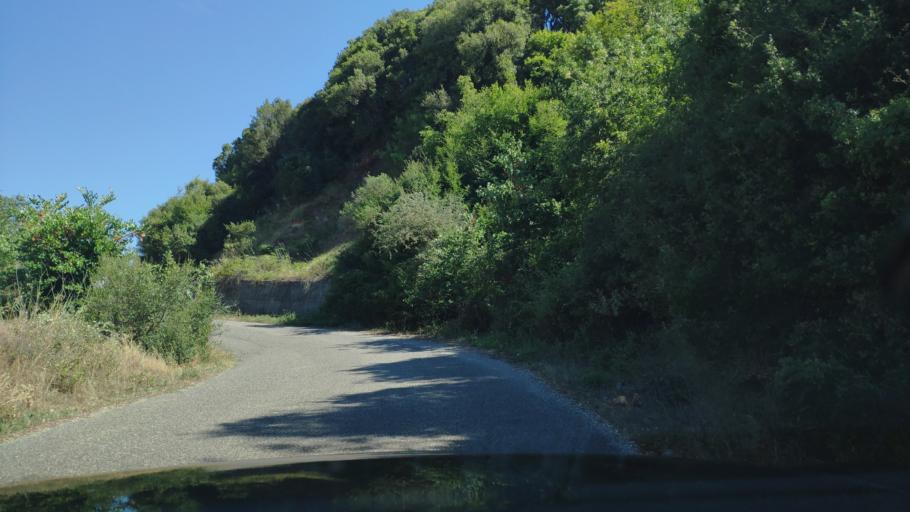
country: GR
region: West Greece
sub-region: Nomos Aitolias kai Akarnanias
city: Katouna
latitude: 38.8227
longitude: 21.1023
